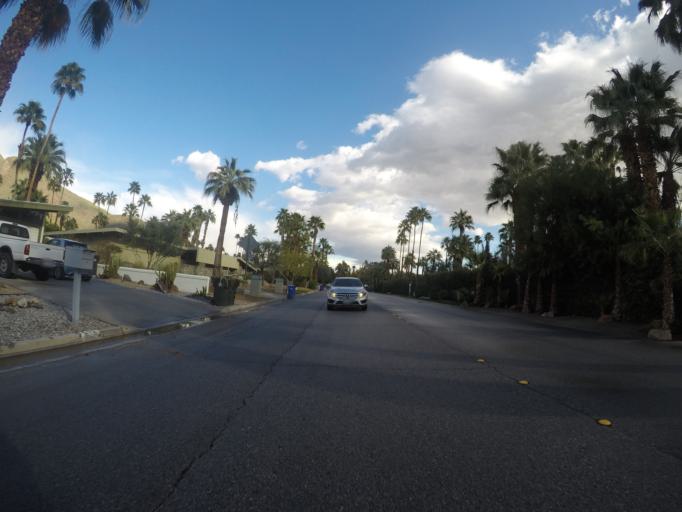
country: US
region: California
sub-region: Riverside County
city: Palm Springs
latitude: 33.8328
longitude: -116.5543
